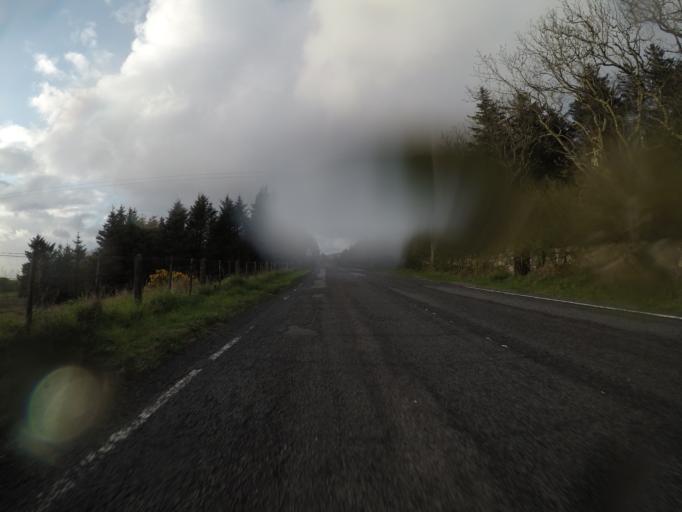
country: GB
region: Scotland
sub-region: Highland
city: Portree
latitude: 57.5684
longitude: -6.3646
